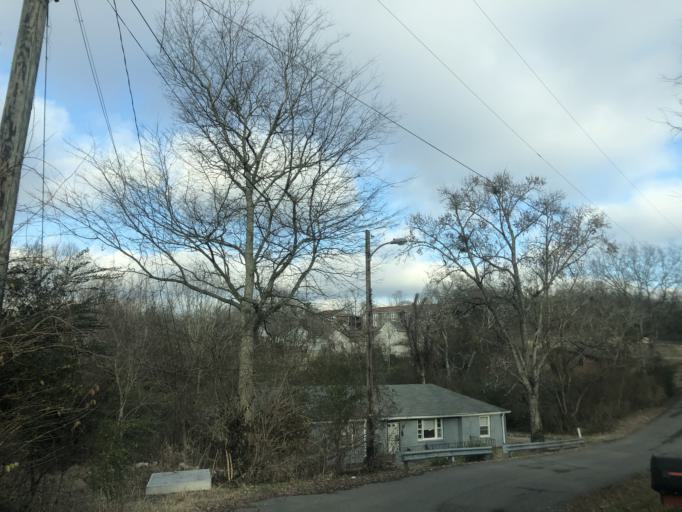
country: US
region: Tennessee
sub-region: Davidson County
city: Nashville
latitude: 36.2134
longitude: -86.7966
